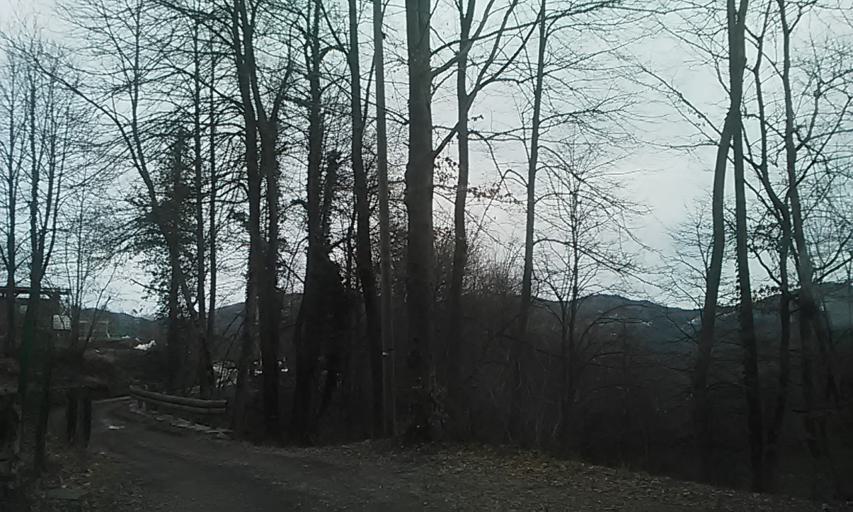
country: IT
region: Piedmont
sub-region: Provincia di Vercelli
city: Quarona
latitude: 45.7835
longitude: 8.2426
